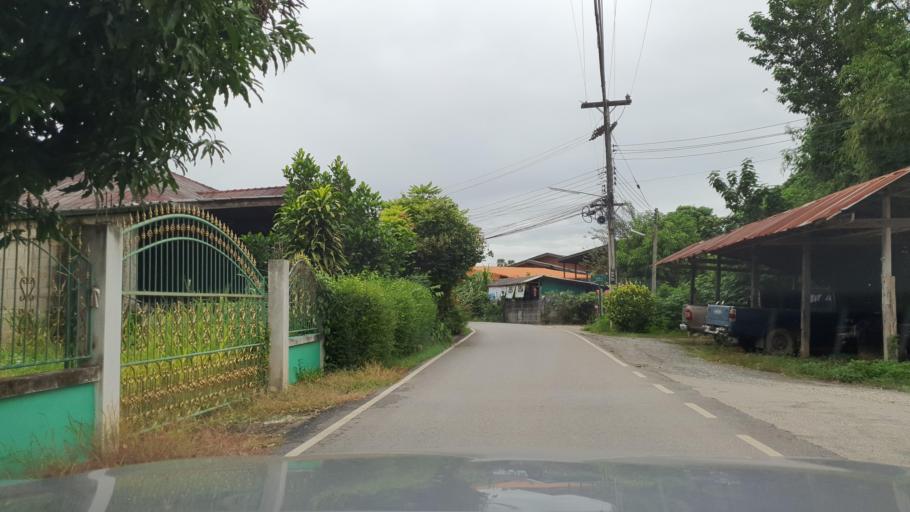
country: TH
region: Lamphun
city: Lamphun
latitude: 18.5973
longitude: 98.9731
